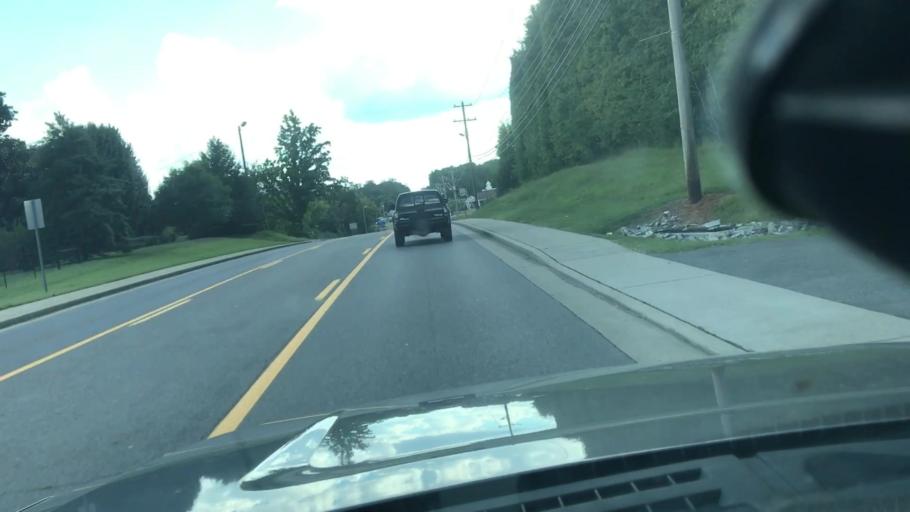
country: US
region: Tennessee
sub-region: Williamson County
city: Fairview
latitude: 35.9774
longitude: -87.1259
